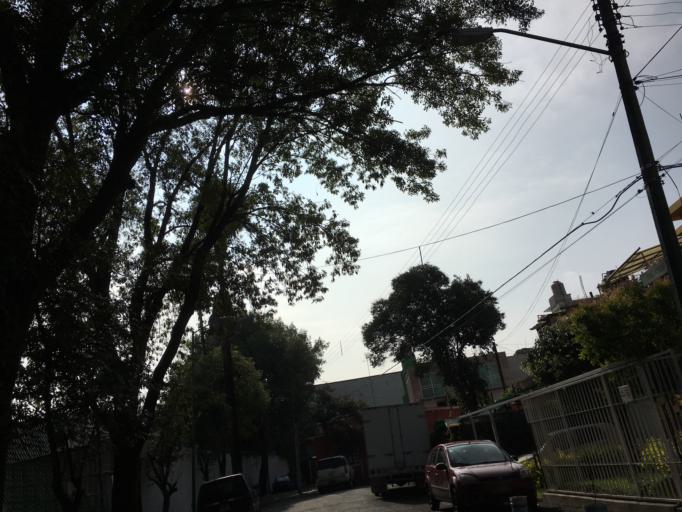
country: MX
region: Mexico City
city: Tlalpan
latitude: 19.2862
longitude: -99.1393
